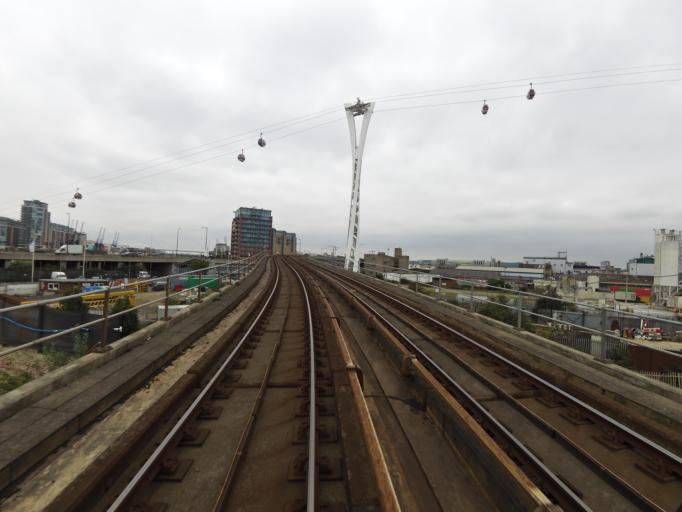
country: GB
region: England
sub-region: Greater London
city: Poplar
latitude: 51.5060
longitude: 0.0141
